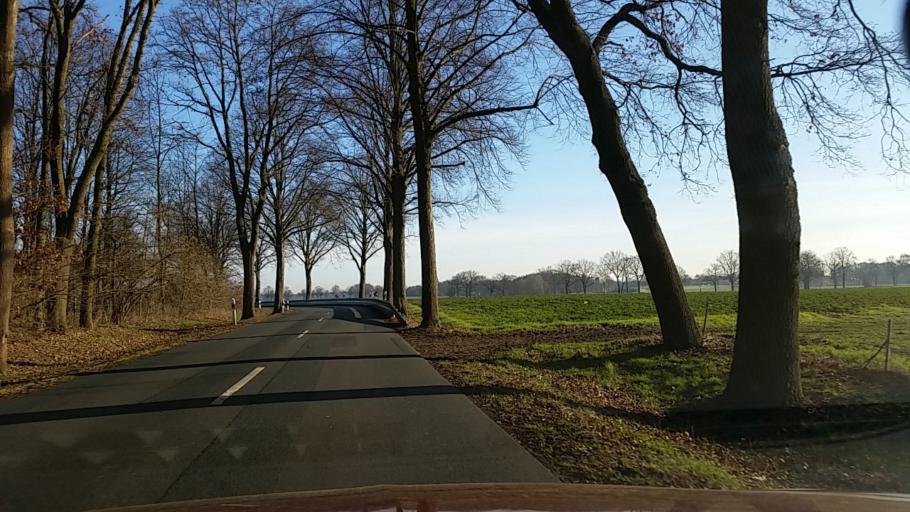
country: DE
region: Lower Saxony
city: Tiddische
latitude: 52.4835
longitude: 10.8228
